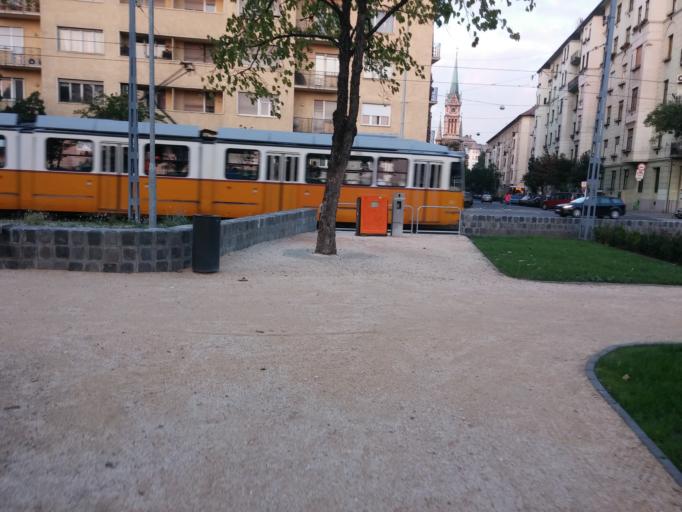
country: HU
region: Budapest
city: Budapest IX. keruelet
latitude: 47.4822
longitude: 19.0634
